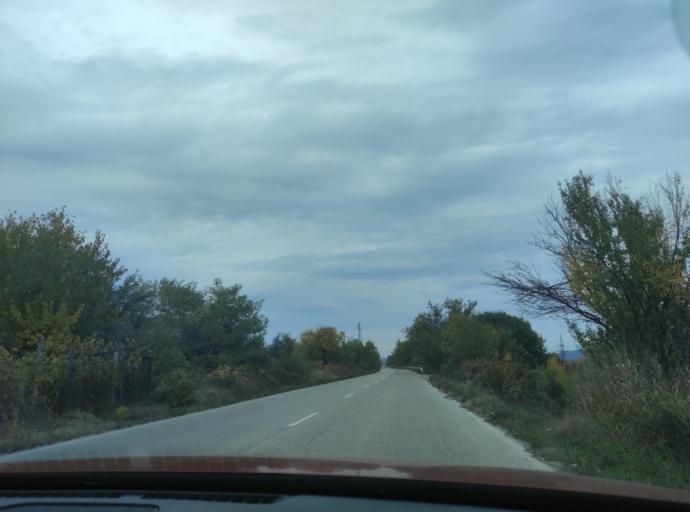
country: BG
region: Montana
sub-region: Obshtina Berkovitsa
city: Berkovitsa
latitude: 43.2111
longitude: 23.1594
